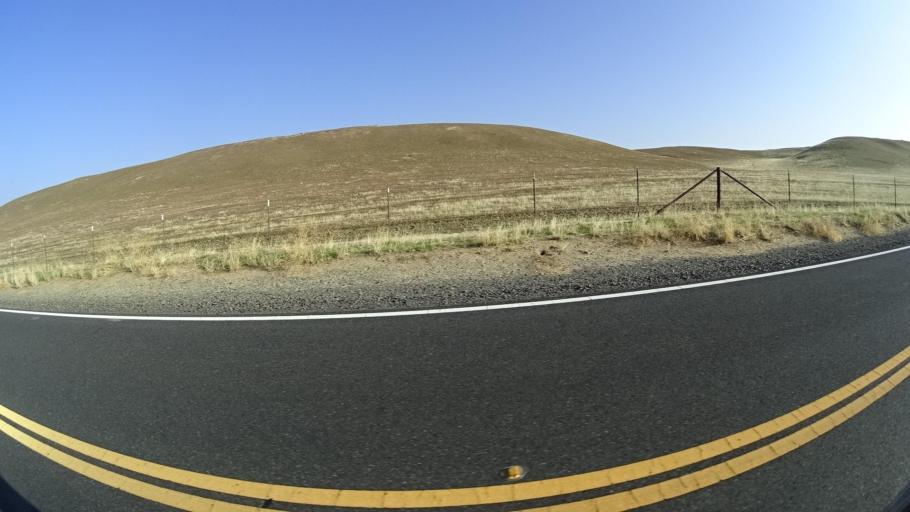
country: US
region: California
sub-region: Tulare County
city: Richgrove
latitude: 35.7455
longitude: -118.9642
